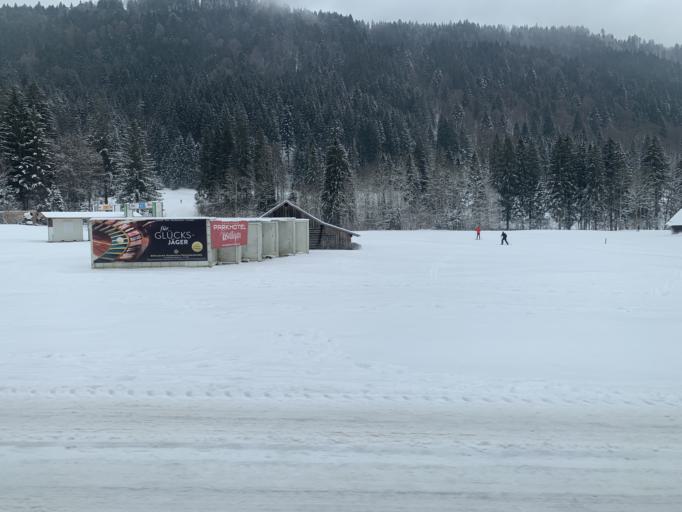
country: DE
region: Bavaria
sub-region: Upper Bavaria
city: Farchant
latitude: 47.4875
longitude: 11.1855
